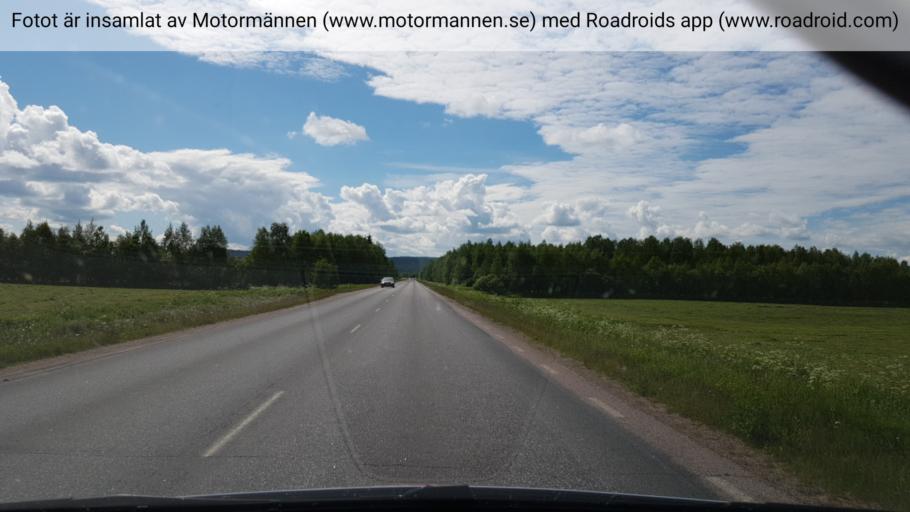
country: SE
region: Norrbotten
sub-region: Overtornea Kommun
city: OEvertornea
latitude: 66.4121
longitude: 23.6234
